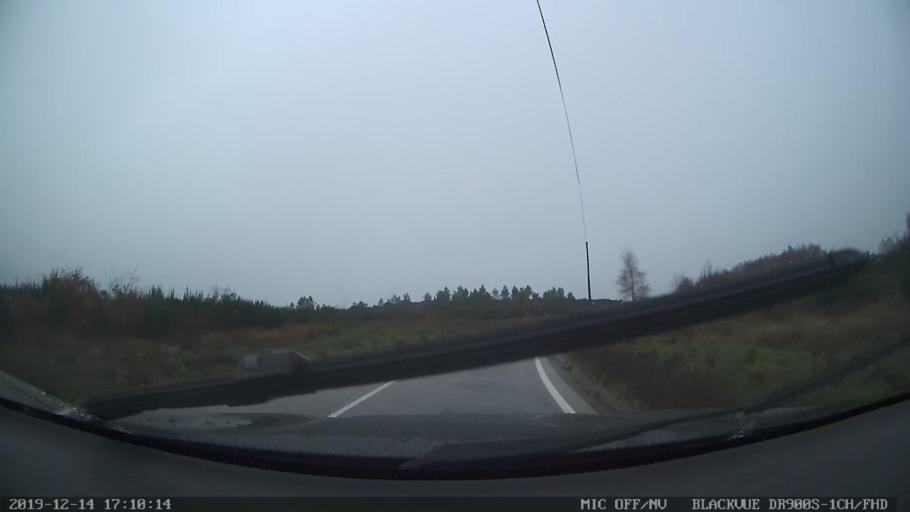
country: PT
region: Vila Real
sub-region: Vila Pouca de Aguiar
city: Vila Pouca de Aguiar
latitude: 41.4792
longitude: -7.6086
